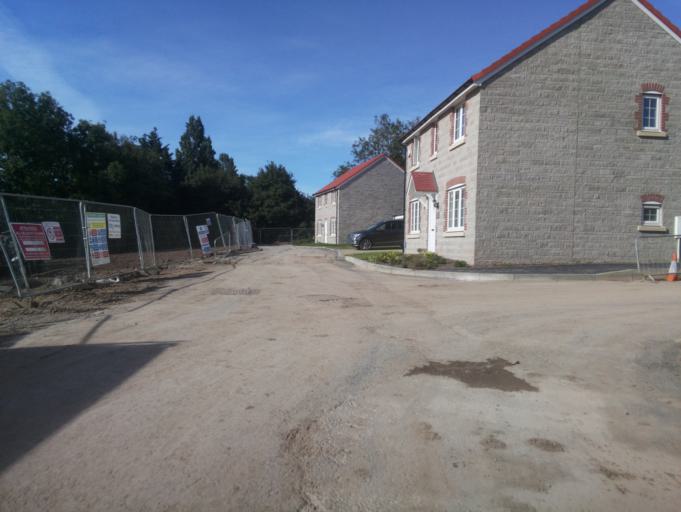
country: GB
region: England
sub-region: Bath and North East Somerset
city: Keynsham
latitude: 51.4013
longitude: -2.5139
